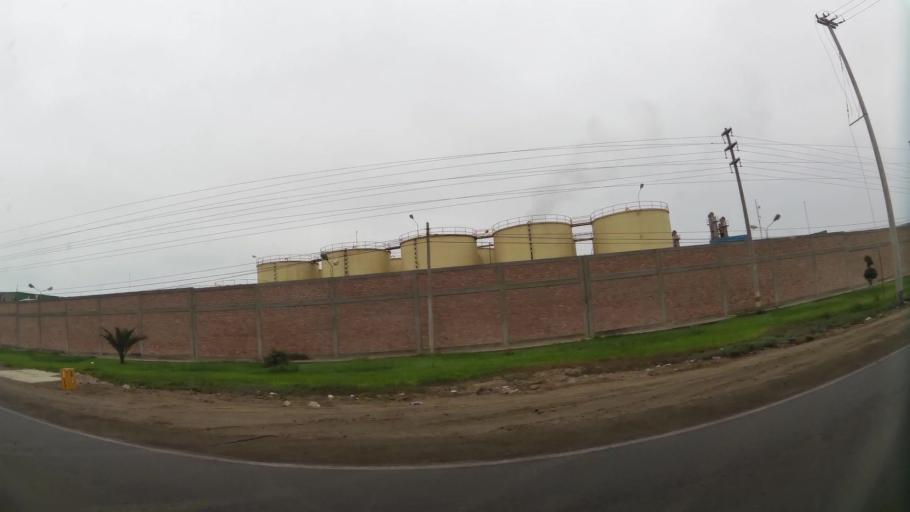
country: PE
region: Ica
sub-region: Provincia de Pisco
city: Paracas
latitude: -13.7896
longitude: -76.2392
